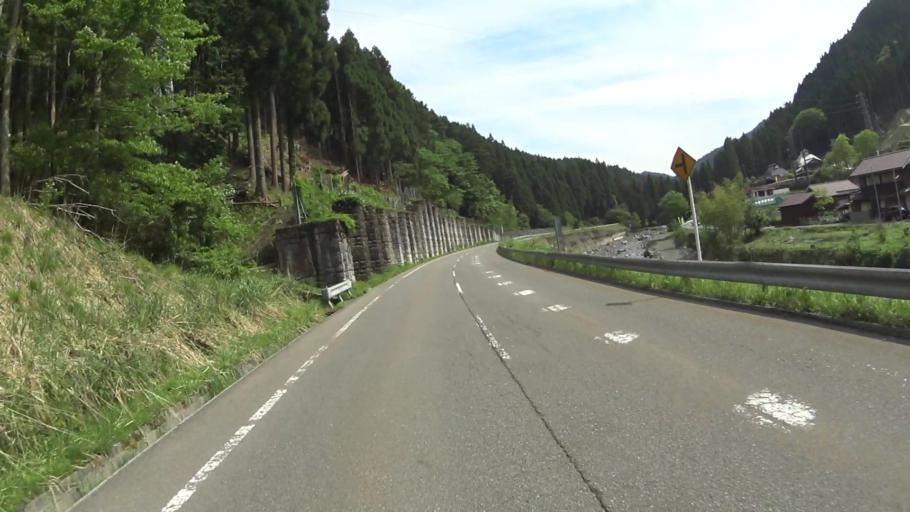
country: JP
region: Shiga Prefecture
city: Kitahama
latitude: 35.2341
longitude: 135.8633
